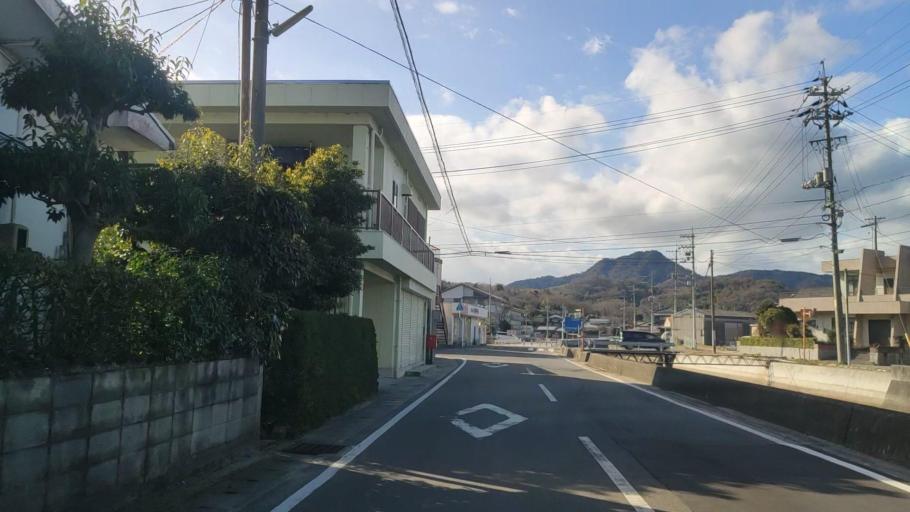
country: JP
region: Hiroshima
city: Innoshima
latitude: 34.2133
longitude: 133.1143
